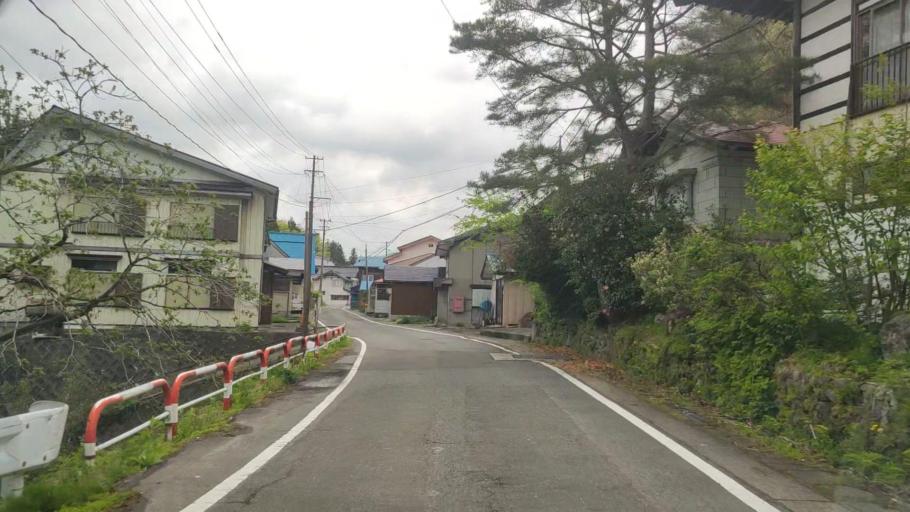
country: JP
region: Fukushima
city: Kitakata
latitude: 37.6759
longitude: 139.6494
